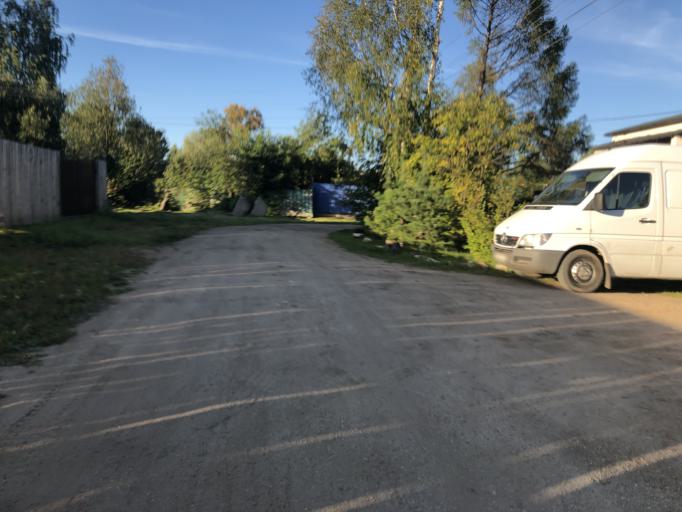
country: RU
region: Tverskaya
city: Rzhev
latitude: 56.2443
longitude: 34.3081
